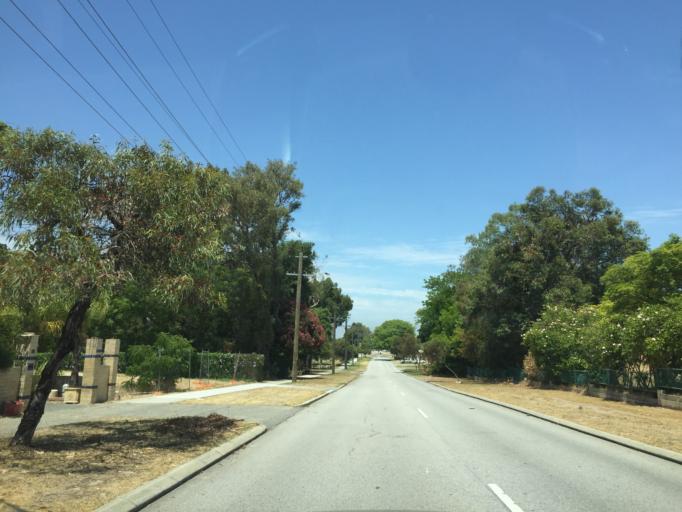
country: AU
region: Western Australia
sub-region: Canning
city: Queens Park
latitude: -32.0008
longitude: 115.9428
